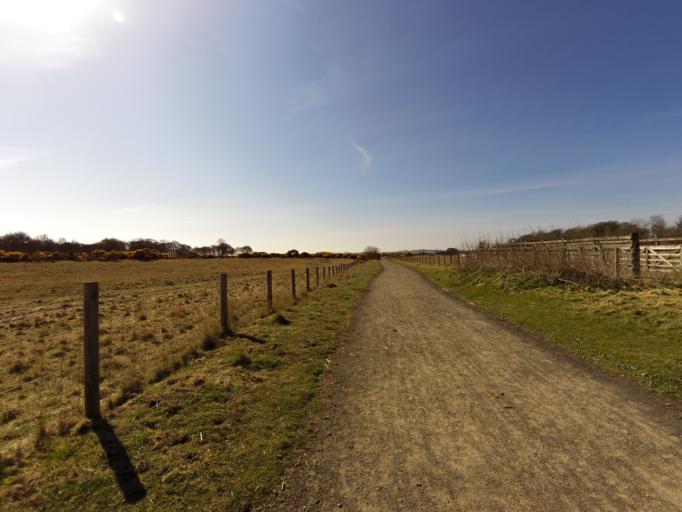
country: GB
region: Scotland
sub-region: Angus
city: Montrose
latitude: 56.7388
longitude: -2.4523
